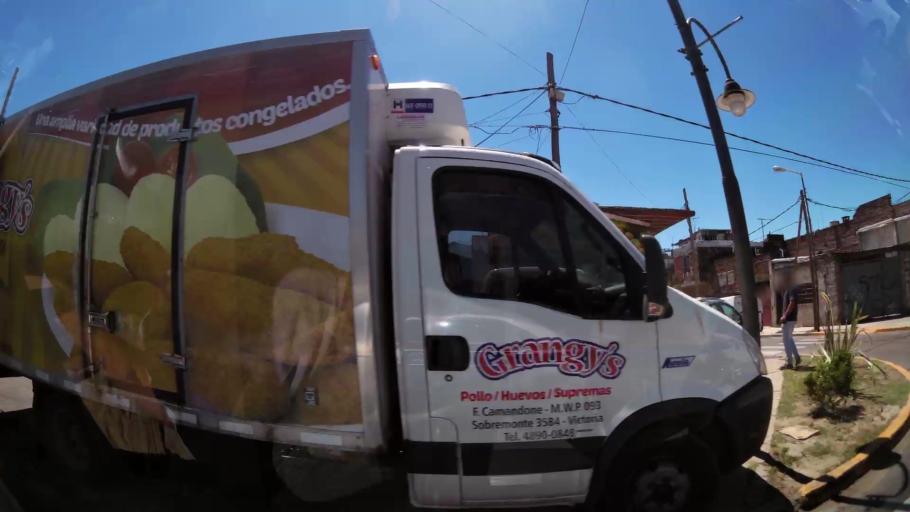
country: AR
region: Buenos Aires
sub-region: Partido de San Isidro
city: San Isidro
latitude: -34.4614
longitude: -58.5478
